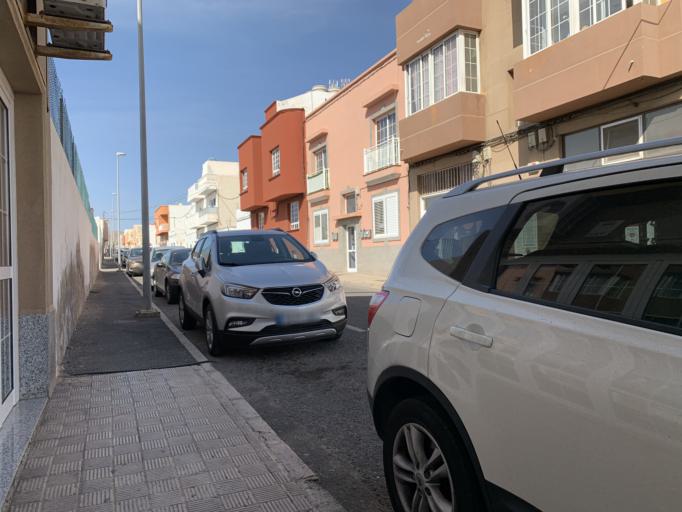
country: ES
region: Canary Islands
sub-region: Provincia de Las Palmas
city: Puerto del Rosario
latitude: 28.4987
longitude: -13.8664
